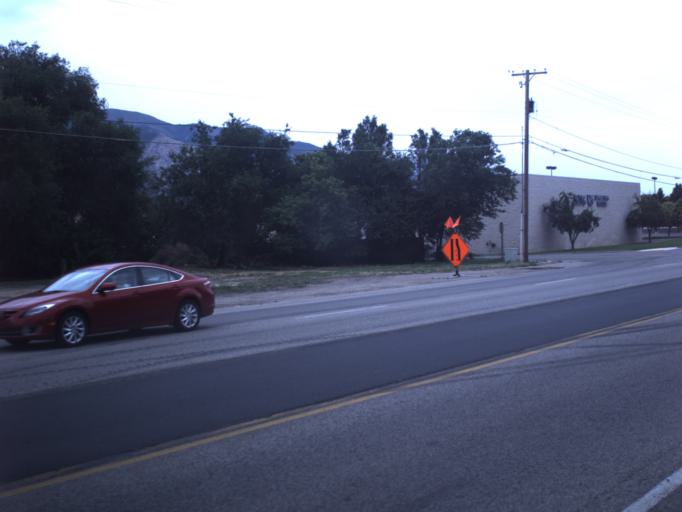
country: US
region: Utah
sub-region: Weber County
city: Ogden
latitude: 41.2484
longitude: -111.9782
